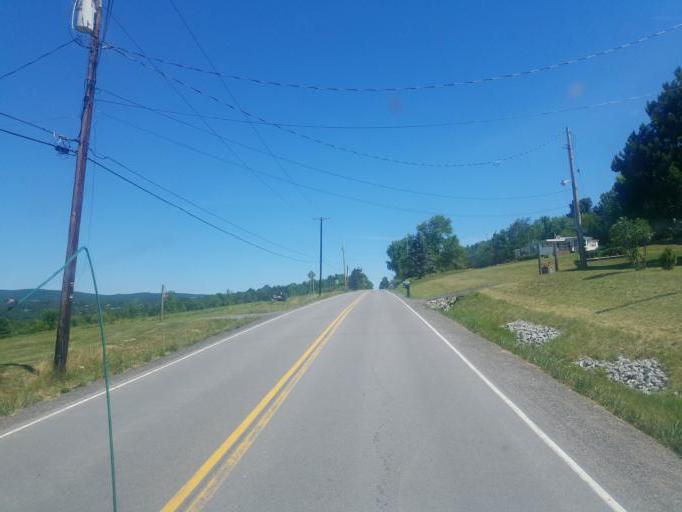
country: US
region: New York
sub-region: Ontario County
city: Naples
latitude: 42.7278
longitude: -77.3249
